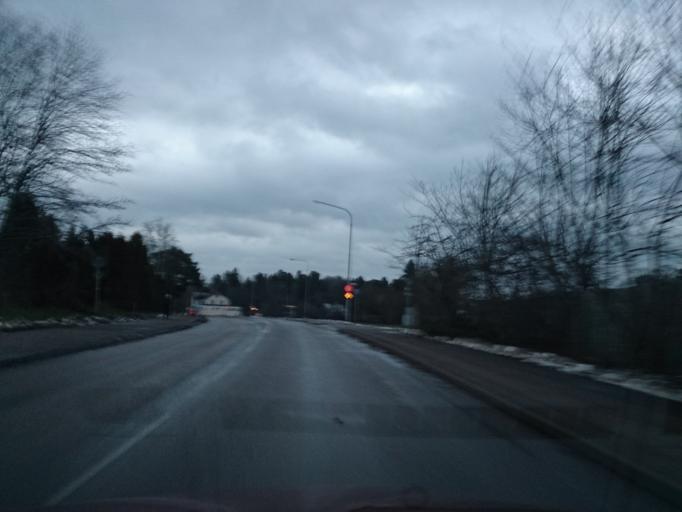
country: SE
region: OEstergoetland
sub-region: Linkopings Kommun
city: Sturefors
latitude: 58.3736
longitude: 15.7074
